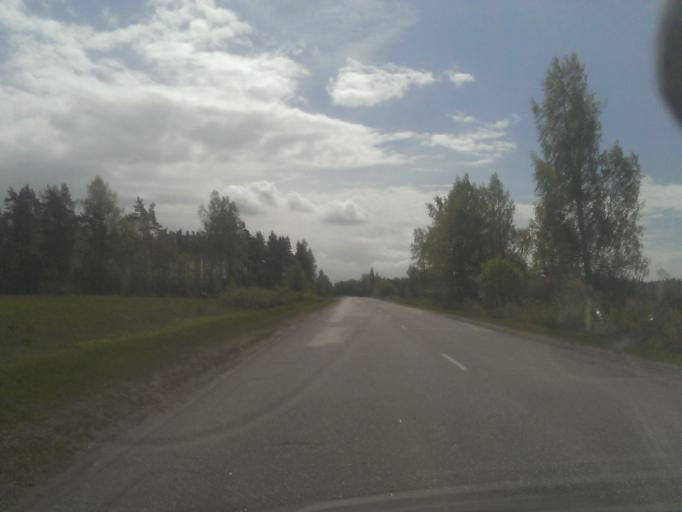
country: LV
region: Ventspils
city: Ventspils
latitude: 57.2976
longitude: 21.5626
